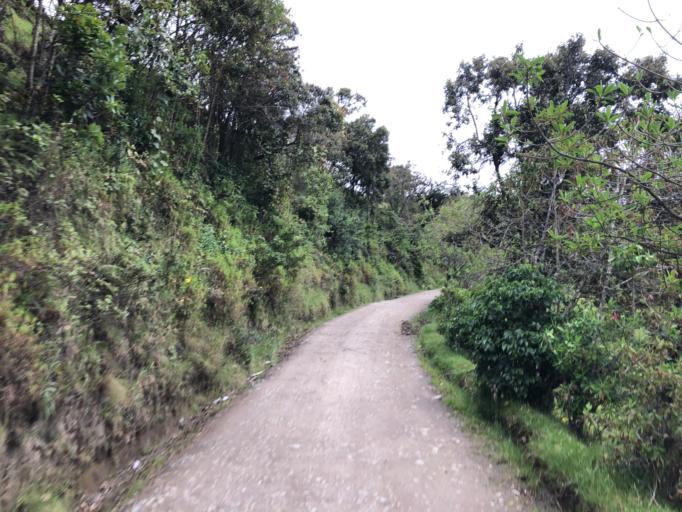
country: CO
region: Cauca
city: Totoro
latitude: 2.5073
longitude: -76.3618
